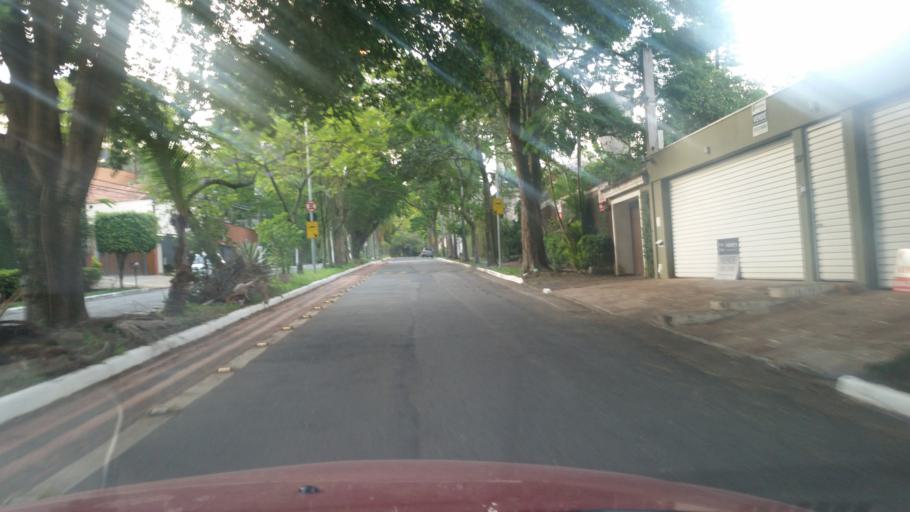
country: BR
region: Sao Paulo
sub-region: Diadema
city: Diadema
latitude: -23.6374
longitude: -46.6827
